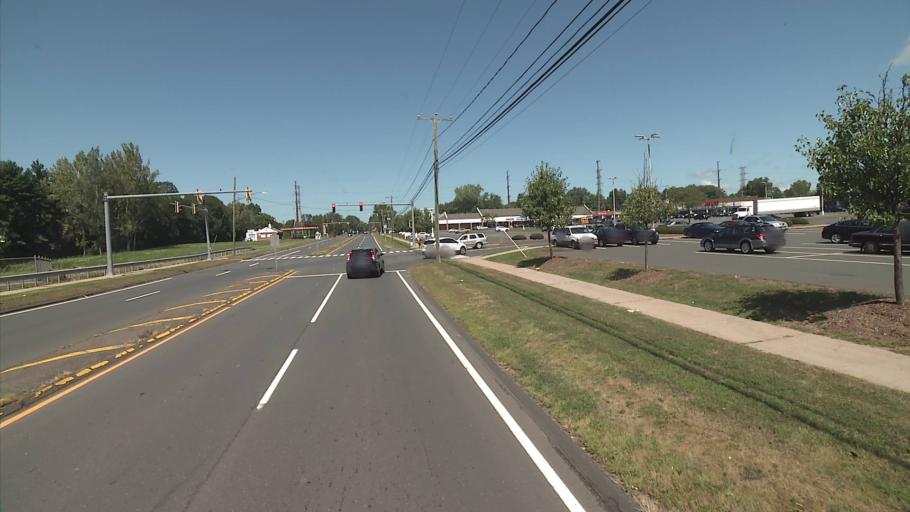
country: US
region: Connecticut
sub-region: Hartford County
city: Windsor
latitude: 41.8197
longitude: -72.6567
